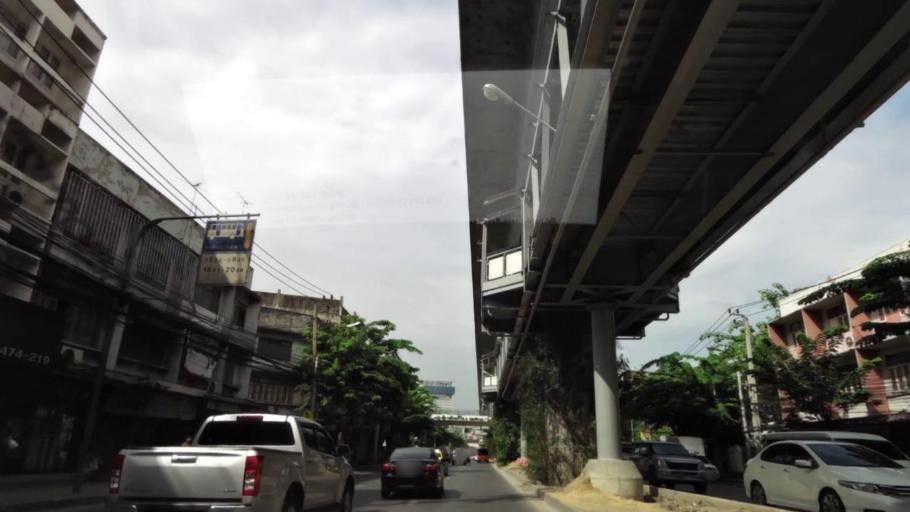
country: TH
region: Bangkok
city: Phra Khanong
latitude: 13.6780
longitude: 100.6088
